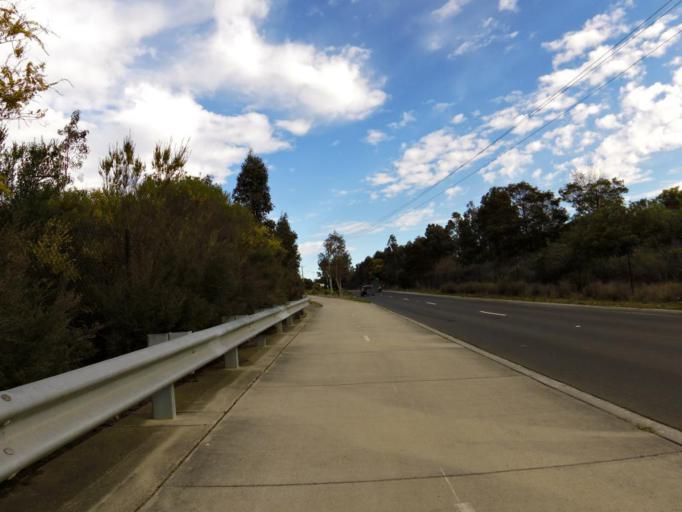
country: AU
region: Victoria
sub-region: Knox
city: Wantirna South
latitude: -37.8864
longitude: 145.2145
